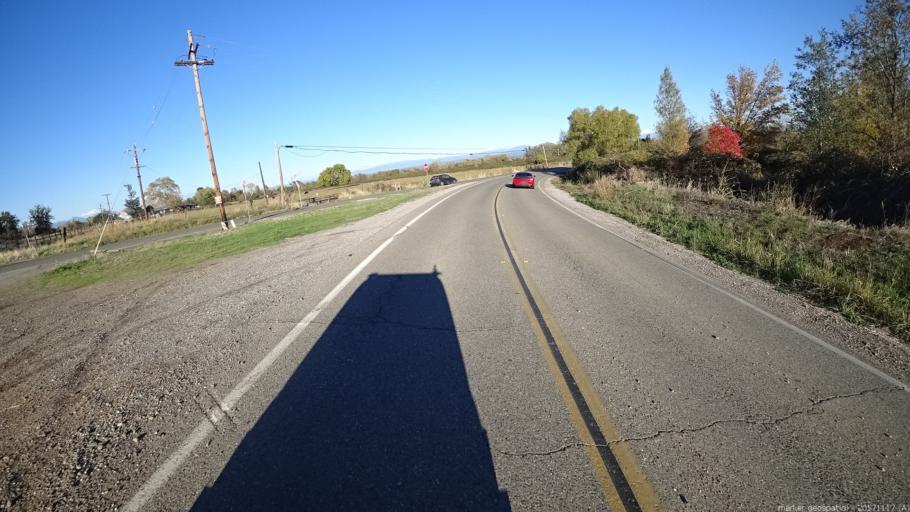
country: US
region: California
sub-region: Shasta County
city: Cottonwood
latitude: 40.4036
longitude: -122.2442
